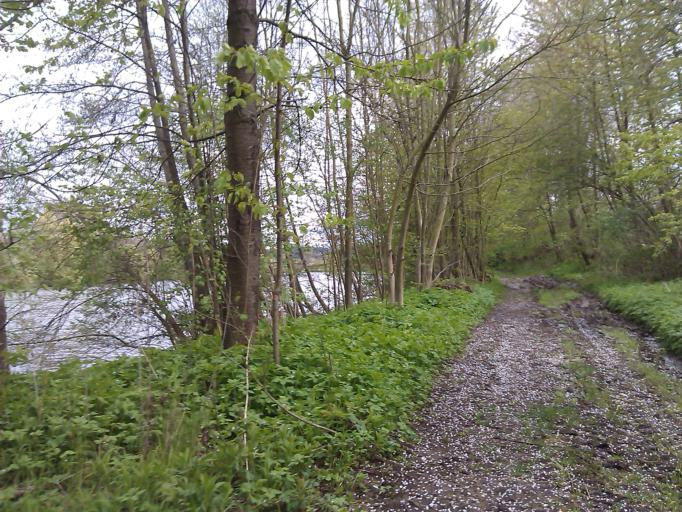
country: DE
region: Baden-Wuerttemberg
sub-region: Regierungsbezirk Stuttgart
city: Lauffen am Neckar
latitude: 49.0933
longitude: 9.1588
